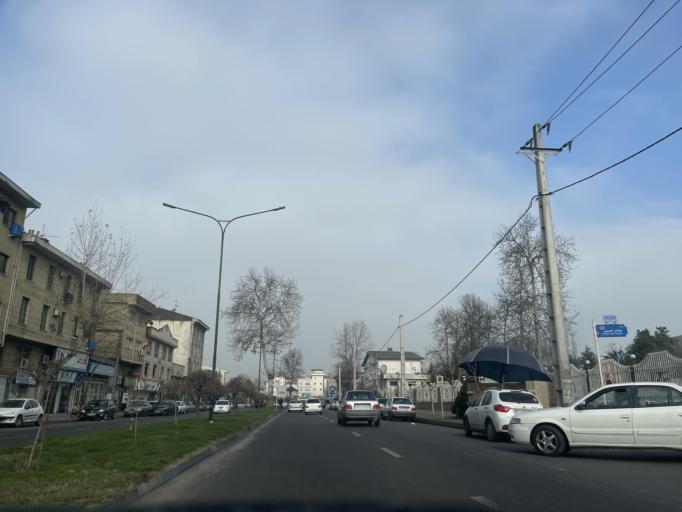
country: IR
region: Gilan
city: Rasht
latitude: 37.2735
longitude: 49.6084
